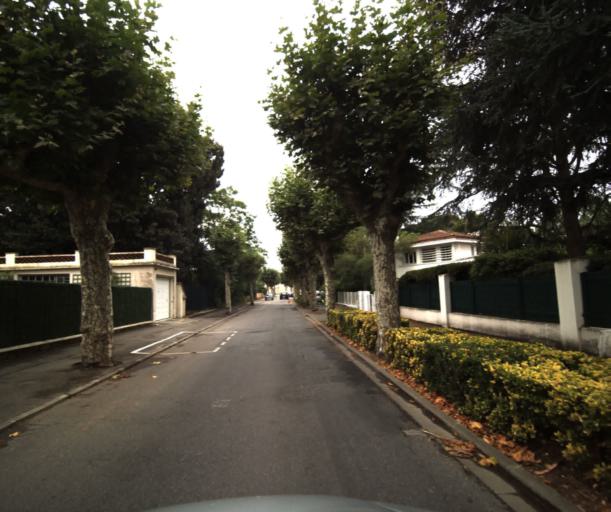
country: FR
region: Midi-Pyrenees
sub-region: Departement de la Haute-Garonne
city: Portet-sur-Garonne
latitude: 43.5231
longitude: 1.4050
